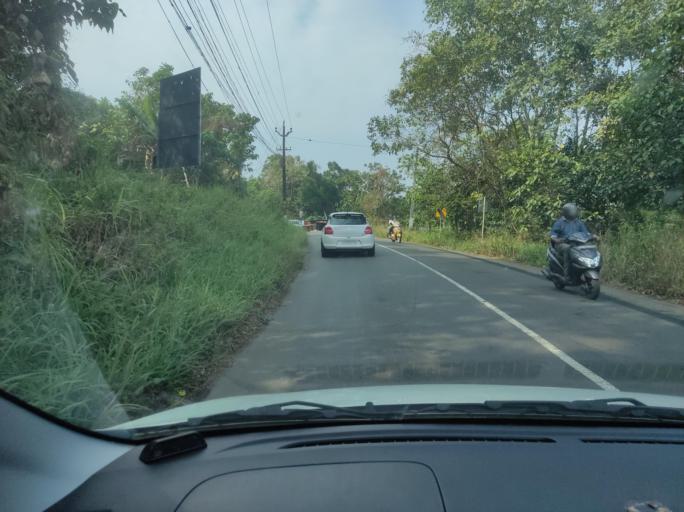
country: IN
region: Kerala
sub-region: Pattanamtitta
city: Adur
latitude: 9.1396
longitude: 76.7303
